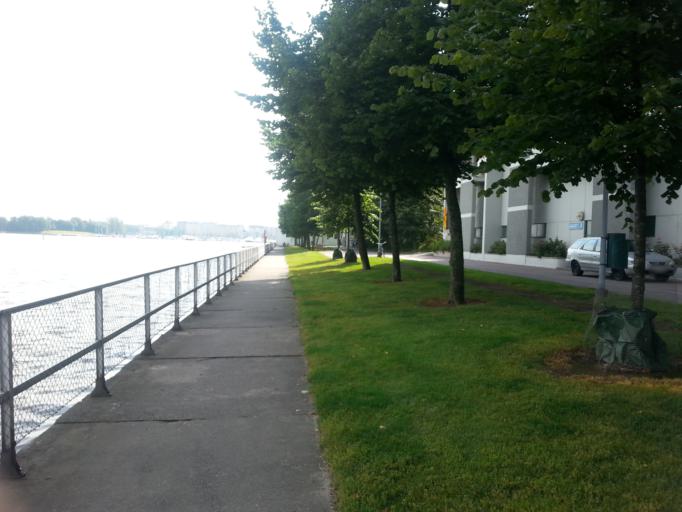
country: FI
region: Uusimaa
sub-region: Helsinki
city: Helsinki
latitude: 60.1795
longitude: 24.9635
